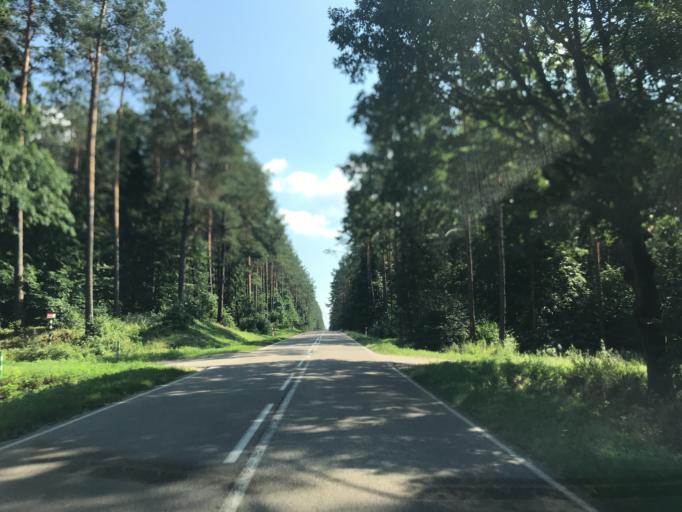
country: PL
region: Warmian-Masurian Voivodeship
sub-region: Powiat dzialdowski
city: Lidzbark
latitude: 53.2254
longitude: 19.8352
